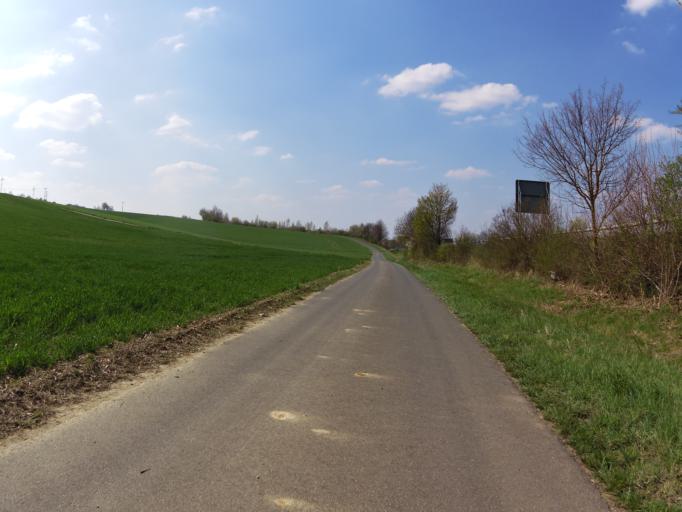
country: DE
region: Bavaria
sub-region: Regierungsbezirk Unterfranken
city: Rottendorf
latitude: 49.7835
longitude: 10.0375
